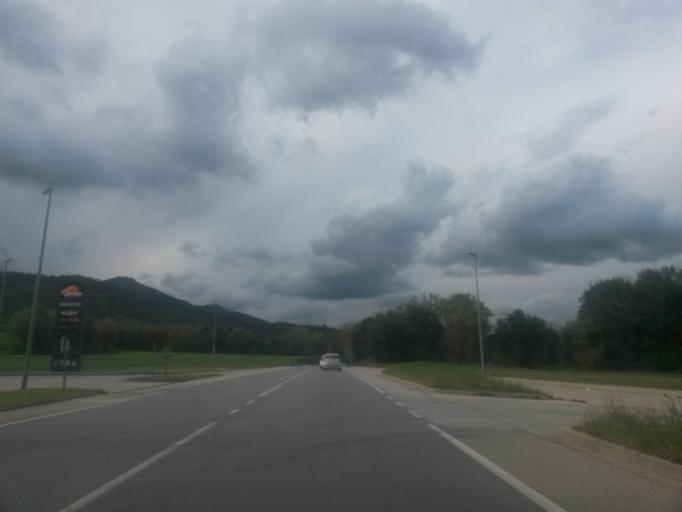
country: ES
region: Catalonia
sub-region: Provincia de Girona
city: Brunyola
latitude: 41.9076
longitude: 2.6614
